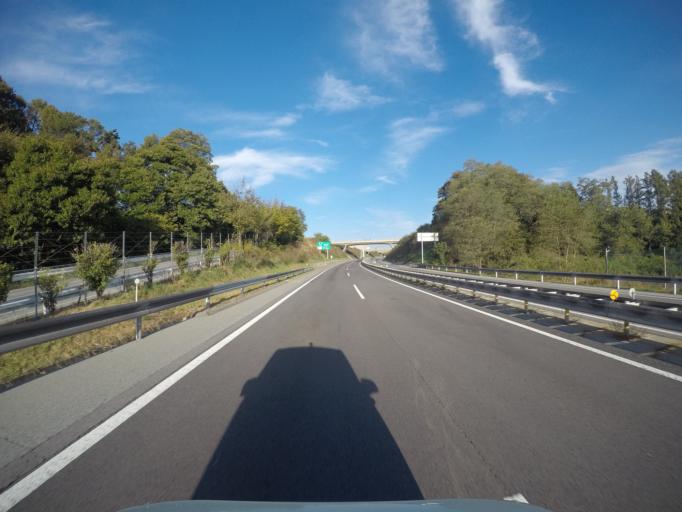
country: JP
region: Nagano
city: Saku
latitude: 36.2817
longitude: 138.4895
